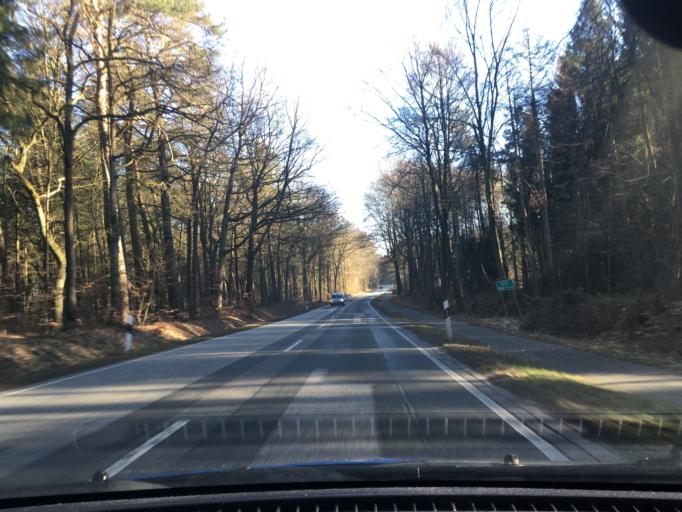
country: DE
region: Schleswig-Holstein
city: Schnakenbek
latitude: 53.3793
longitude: 10.5131
